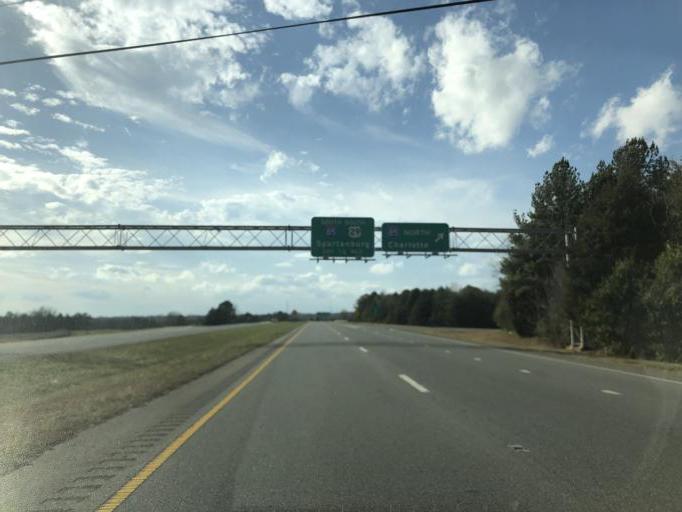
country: US
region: North Carolina
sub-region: Gaston County
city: Bessemer City
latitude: 35.2493
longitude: -81.2941
